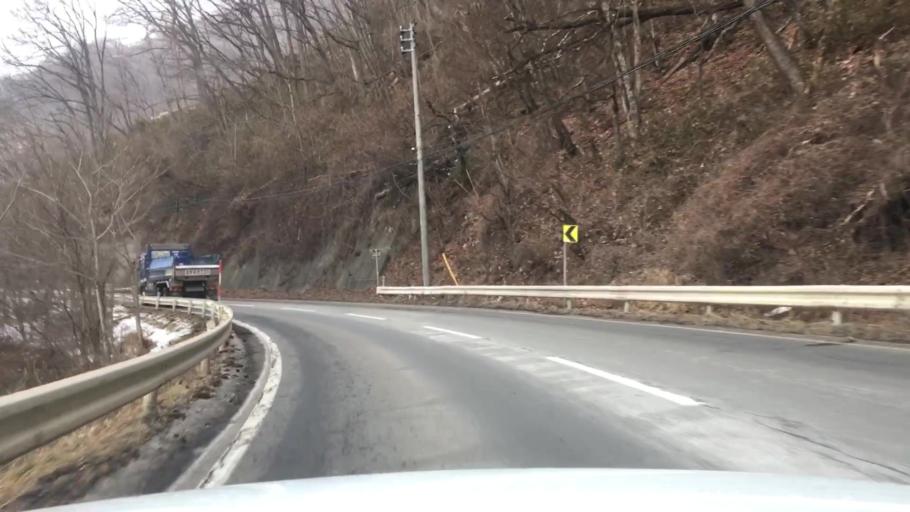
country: JP
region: Iwate
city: Tono
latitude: 39.6217
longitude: 141.4760
